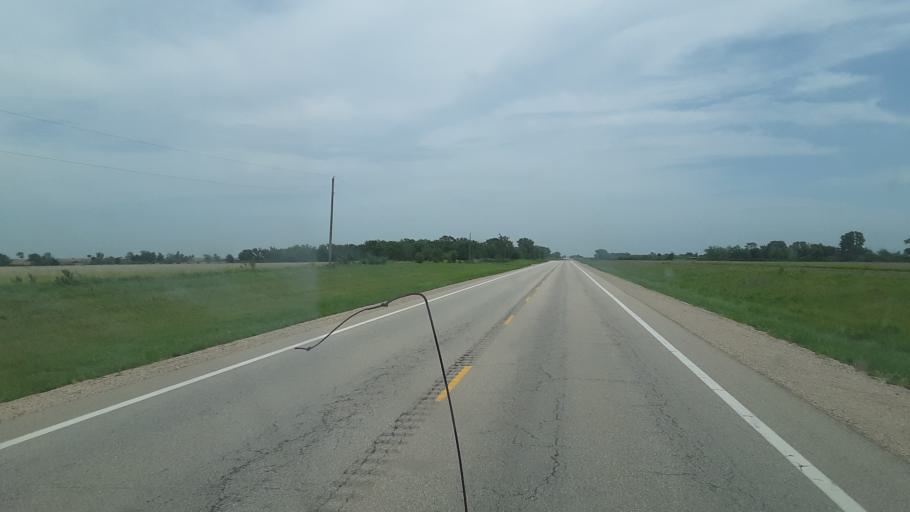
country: US
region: Kansas
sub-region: Woodson County
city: Yates Center
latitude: 37.8362
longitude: -95.8801
